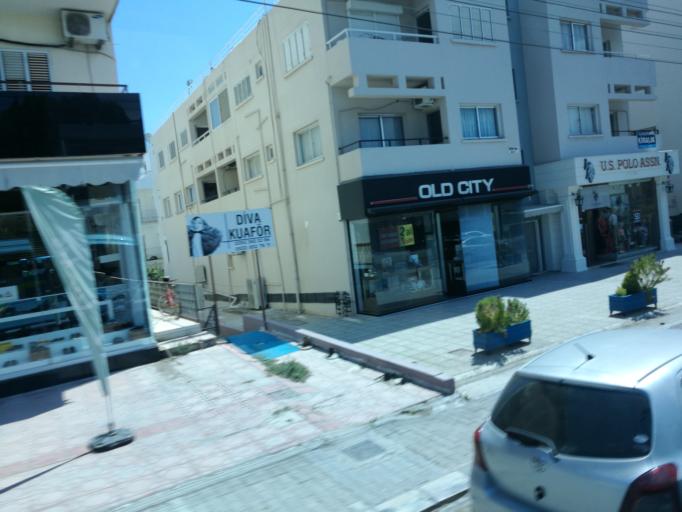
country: CY
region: Ammochostos
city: Famagusta
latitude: 35.1355
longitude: 33.9219
